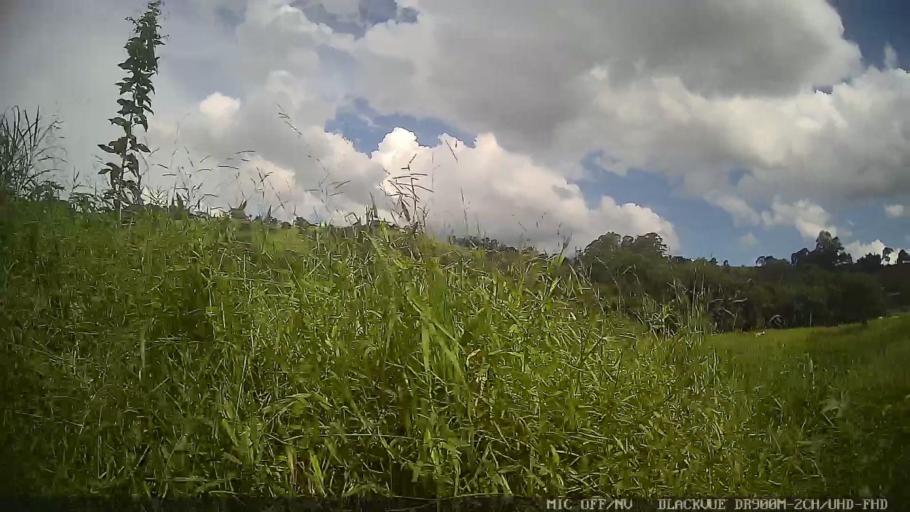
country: BR
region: Minas Gerais
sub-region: Extrema
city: Extrema
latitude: -22.8390
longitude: -46.2483
